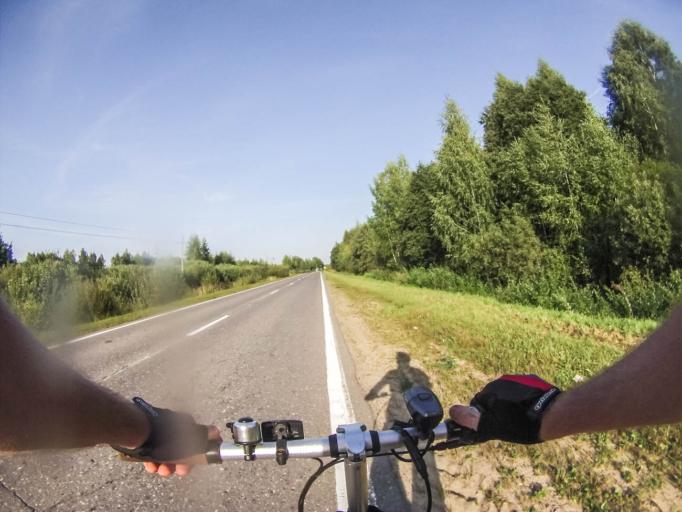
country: RU
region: Jaroslavl
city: Myshkin
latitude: 57.7090
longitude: 38.3676
